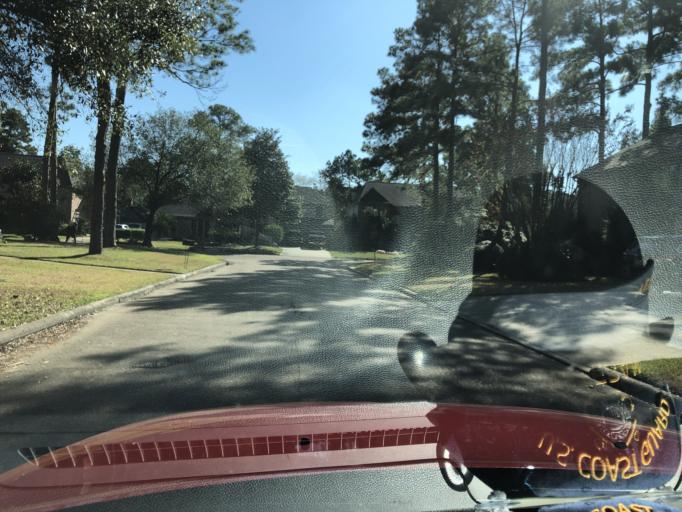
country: US
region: Texas
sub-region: Harris County
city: Tomball
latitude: 30.0217
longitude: -95.5487
